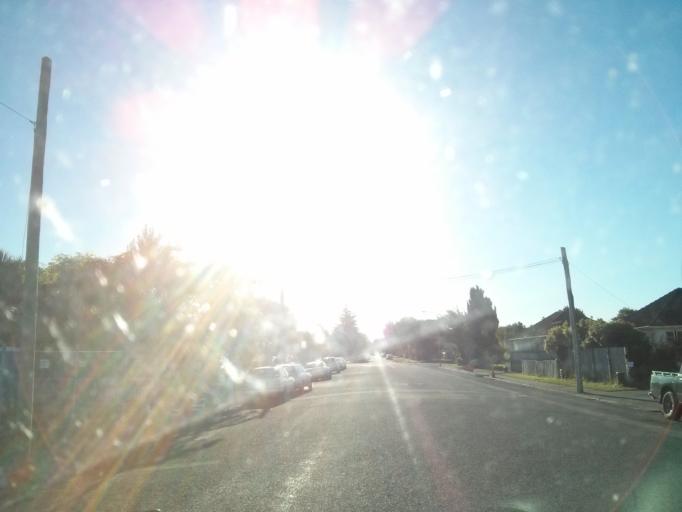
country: NZ
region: Canterbury
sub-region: Christchurch City
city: Christchurch
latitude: -43.5356
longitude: 172.5949
